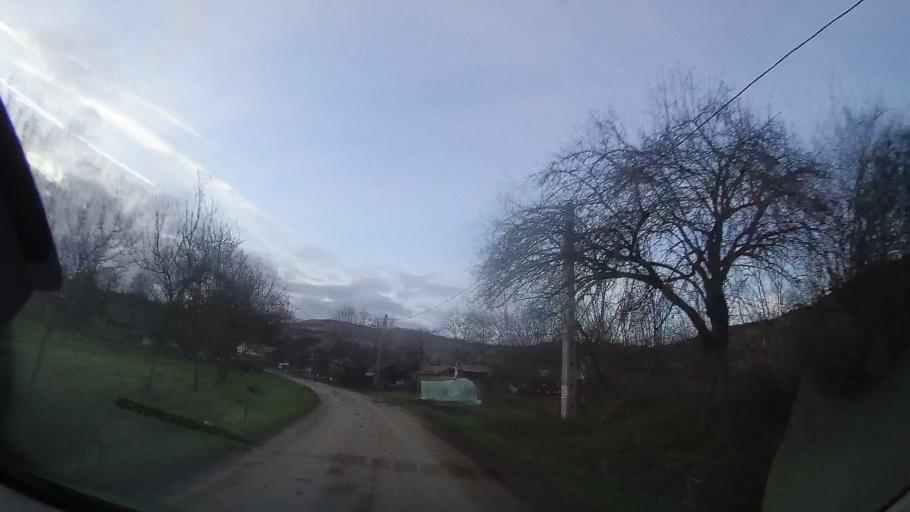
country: RO
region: Cluj
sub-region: Comuna Mociu
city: Mociu
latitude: 46.8566
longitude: 24.0426
